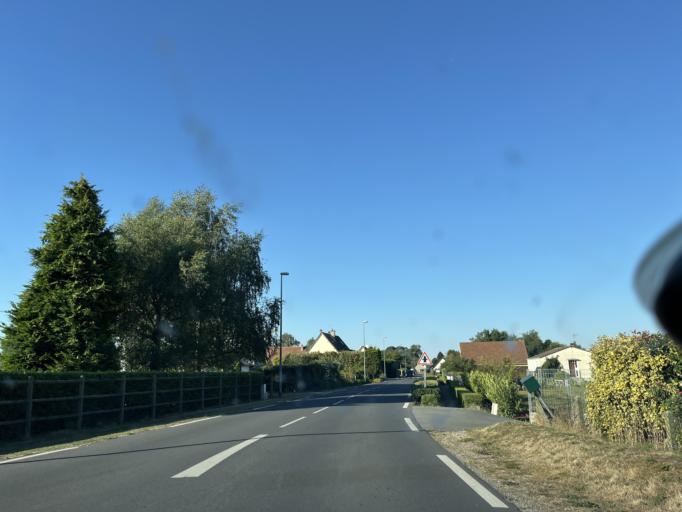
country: FR
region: Haute-Normandie
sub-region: Departement de la Seine-Maritime
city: Lillebonne
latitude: 49.5460
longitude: 0.5607
